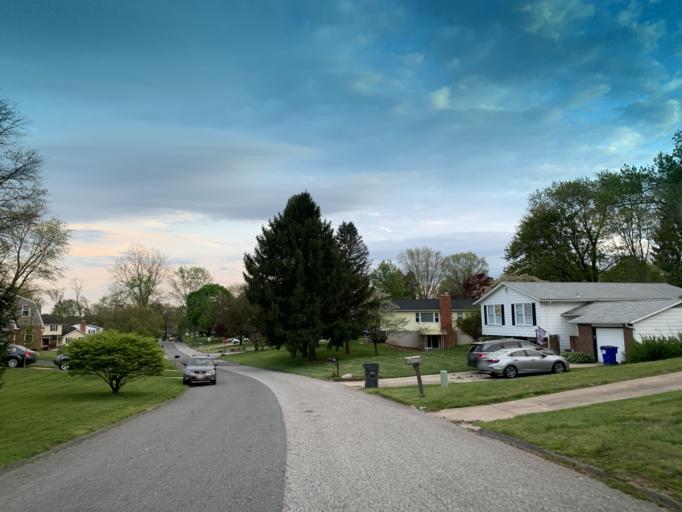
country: US
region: Maryland
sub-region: Harford County
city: Bel Air South
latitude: 39.5070
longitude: -76.3456
